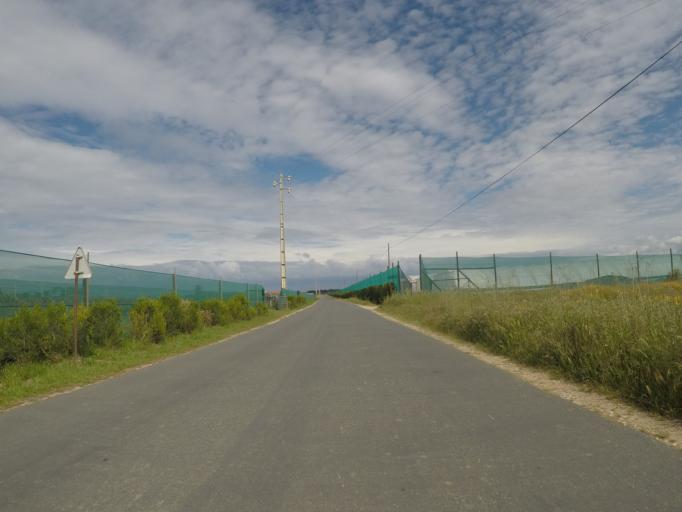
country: PT
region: Beja
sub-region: Odemira
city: Sao Teotonio
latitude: 37.4833
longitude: -8.7696
